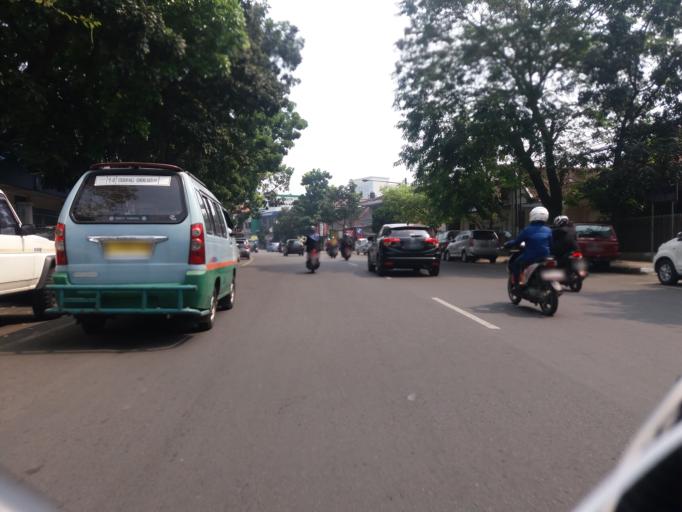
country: ID
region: West Java
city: Bandung
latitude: -6.9075
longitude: 107.6071
